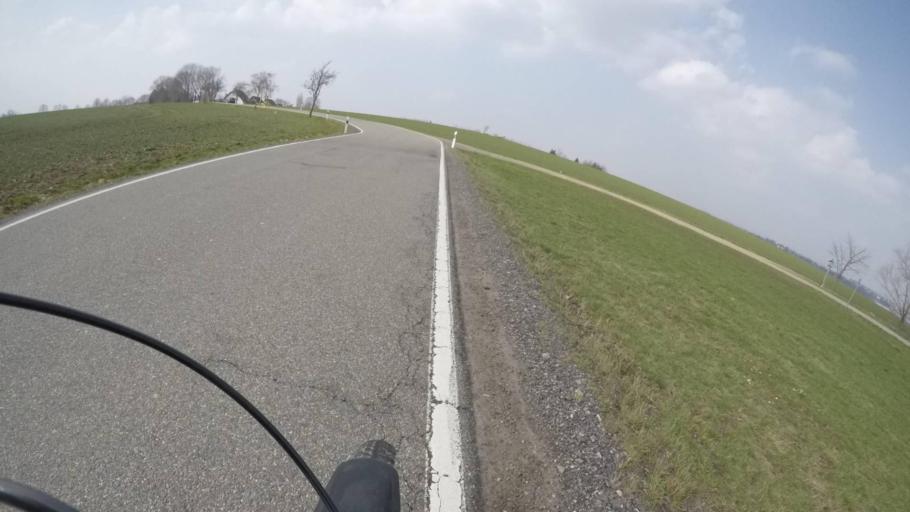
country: DE
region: Saxony
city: Limbach-Oberfrohna
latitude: 50.8337
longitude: 12.7348
